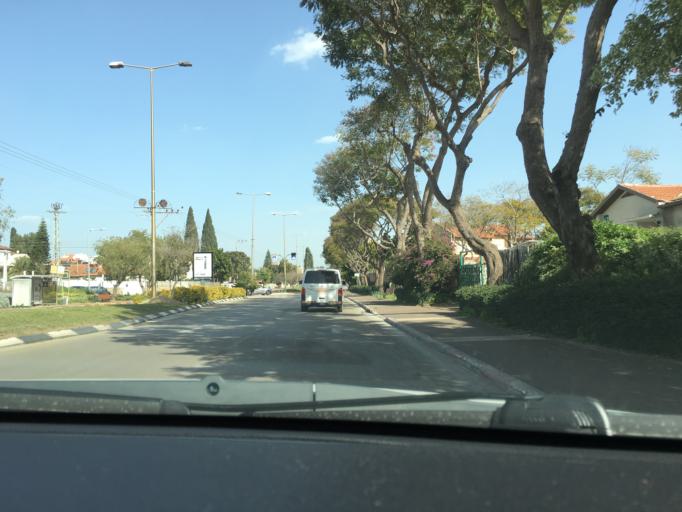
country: IL
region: Central District
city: Kfar Saba
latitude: 32.1821
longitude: 34.8989
